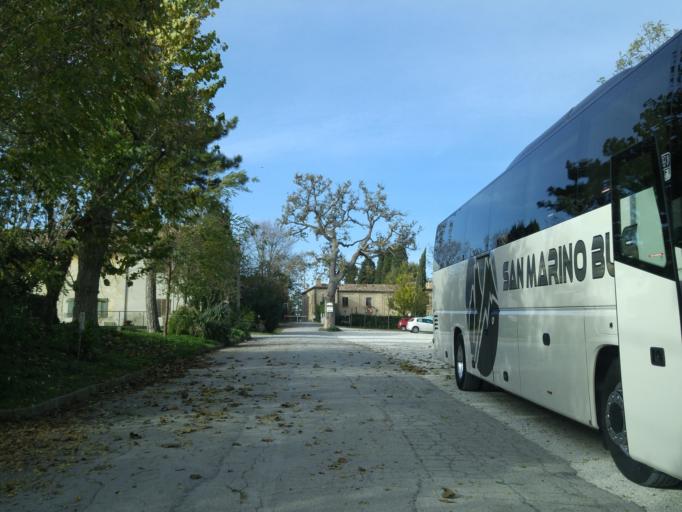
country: IT
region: The Marches
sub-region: Provincia di Pesaro e Urbino
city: Saltara
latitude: 43.7553
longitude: 12.8916
